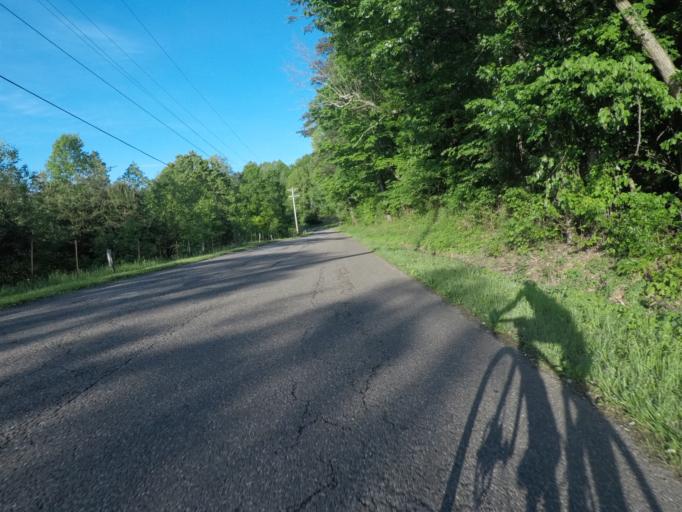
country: US
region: West Virginia
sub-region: Cabell County
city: Huntington
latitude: 38.5509
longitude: -82.4279
